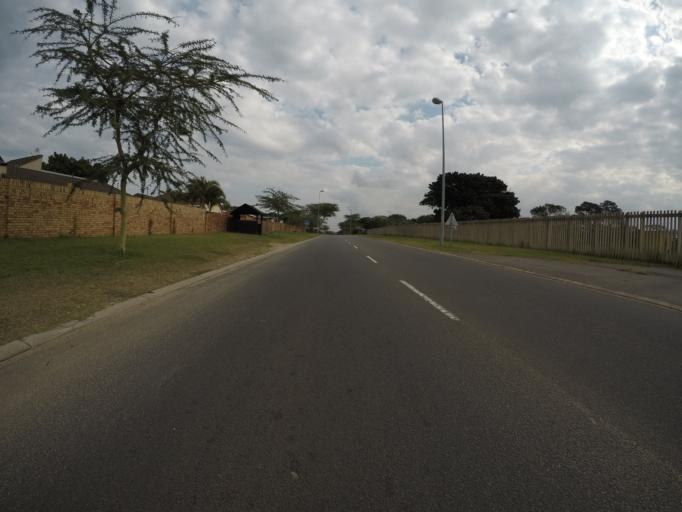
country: ZA
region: KwaZulu-Natal
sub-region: uThungulu District Municipality
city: Richards Bay
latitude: -28.7370
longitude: 32.0834
